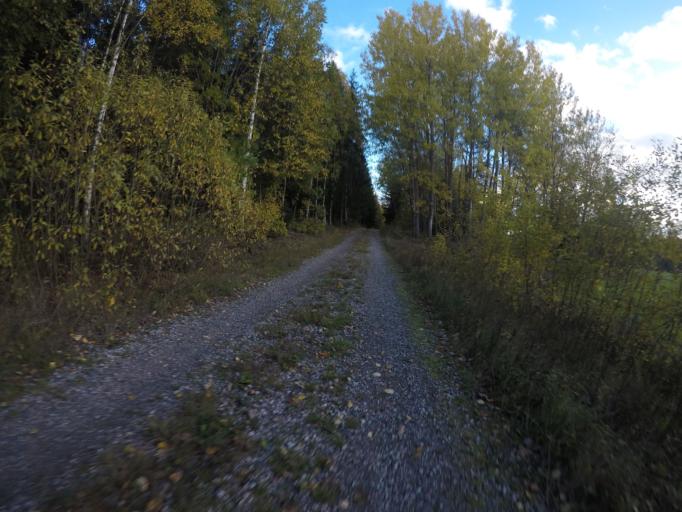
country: SE
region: Vaestmanland
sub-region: Arboga Kommun
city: Tyringe
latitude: 59.3177
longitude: 15.9781
